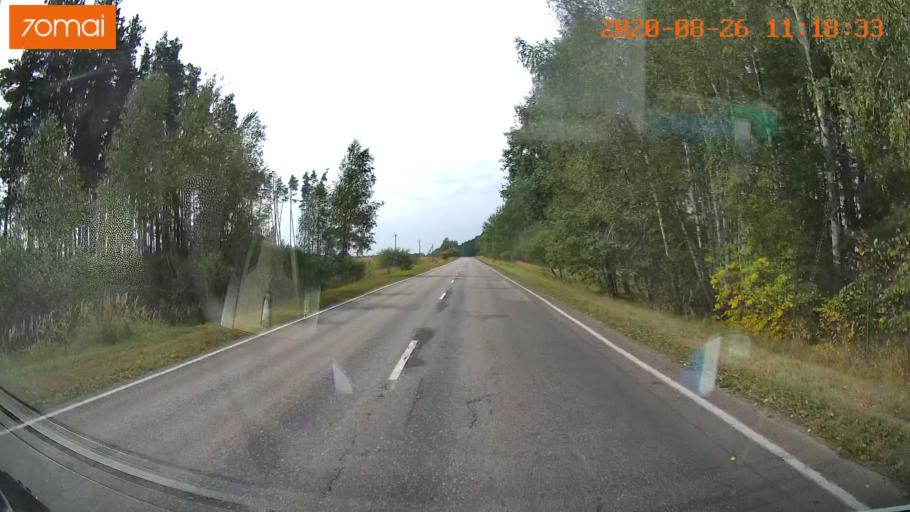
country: RU
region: Rjazan
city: Shilovo
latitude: 54.4088
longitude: 41.0954
